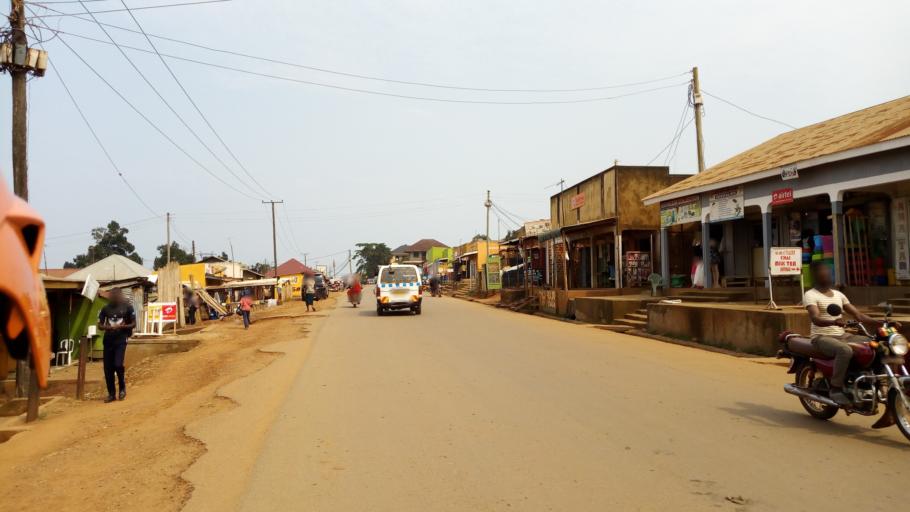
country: UG
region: Central Region
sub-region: Wakiso District
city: Kireka
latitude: 0.3137
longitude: 32.6513
